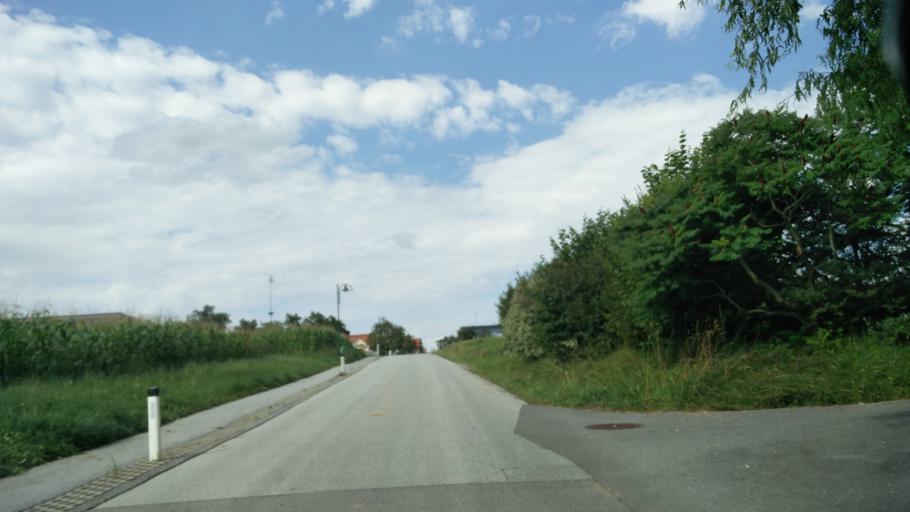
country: AT
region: Styria
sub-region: Politischer Bezirk Weiz
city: Weiz
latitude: 47.2149
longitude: 15.6067
